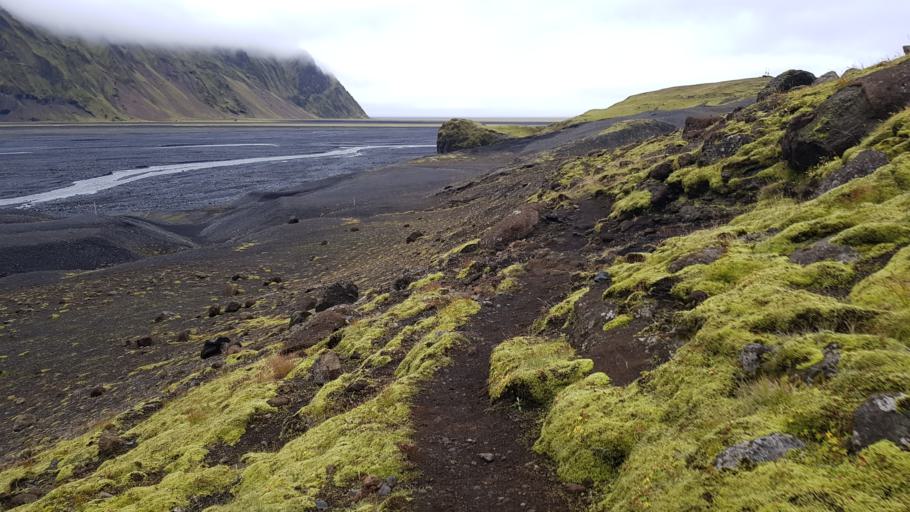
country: IS
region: South
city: Vestmannaeyjar
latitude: 63.5299
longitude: -18.8488
